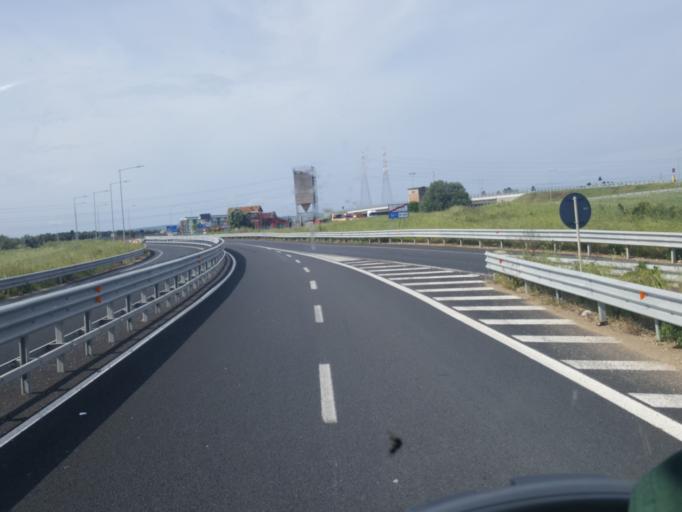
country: IT
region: Latium
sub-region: Citta metropolitana di Roma Capitale
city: Aurelia
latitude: 42.1613
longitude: 11.7884
